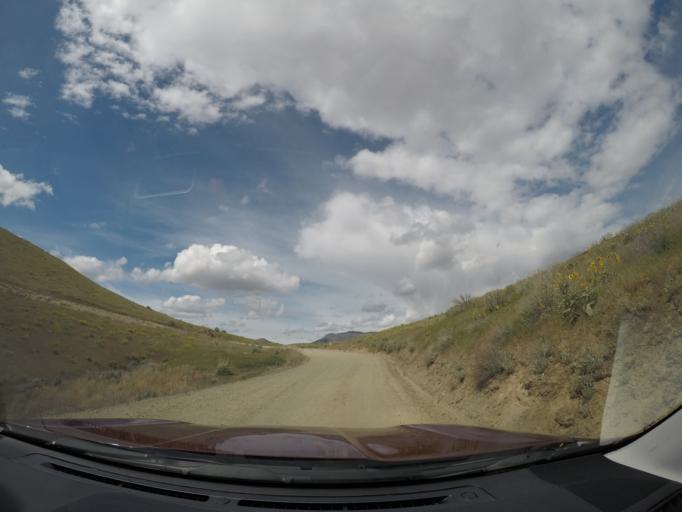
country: US
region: Washington
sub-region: Chelan County
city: West Wenatchee
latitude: 47.4623
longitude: -120.3605
